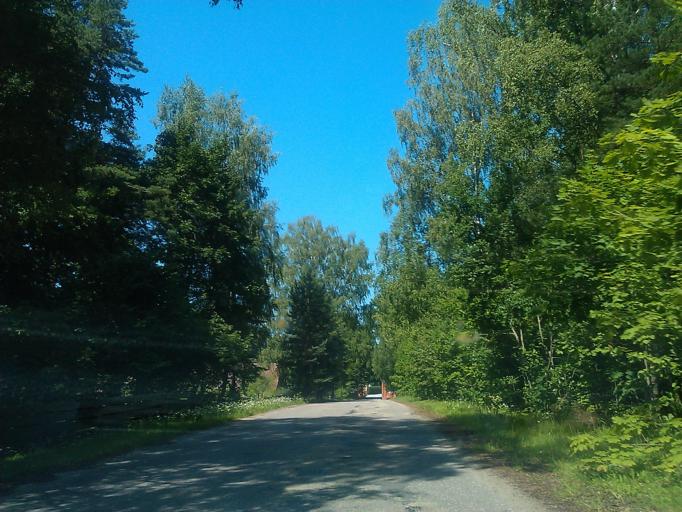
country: LV
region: Saulkrastu
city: Saulkrasti
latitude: 57.4022
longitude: 24.4269
